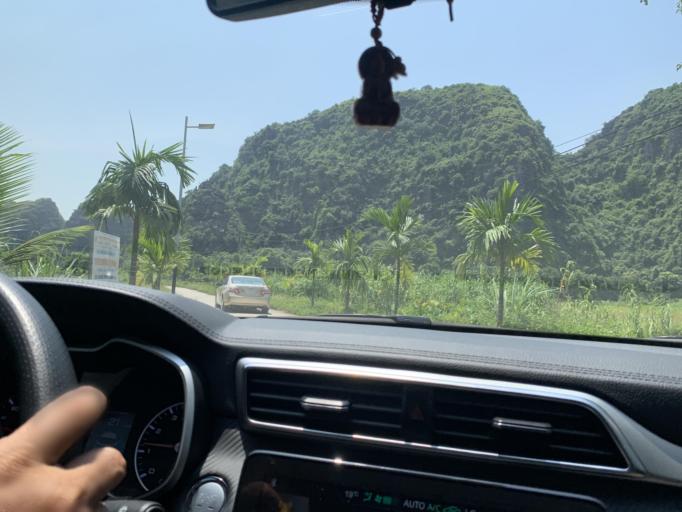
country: VN
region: Ninh Binh
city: Thanh Pho Ninh Binh
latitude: 20.2237
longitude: 105.9301
